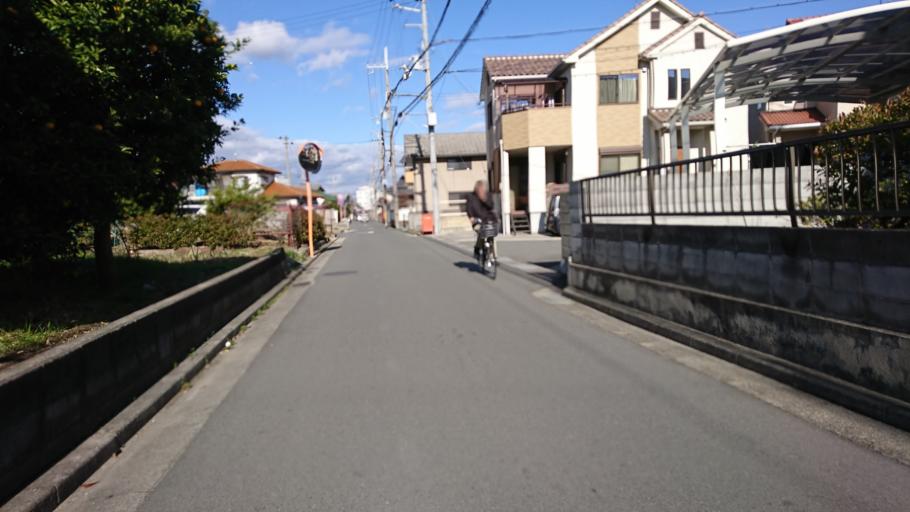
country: JP
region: Hyogo
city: Kakogawacho-honmachi
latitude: 34.7723
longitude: 134.7738
